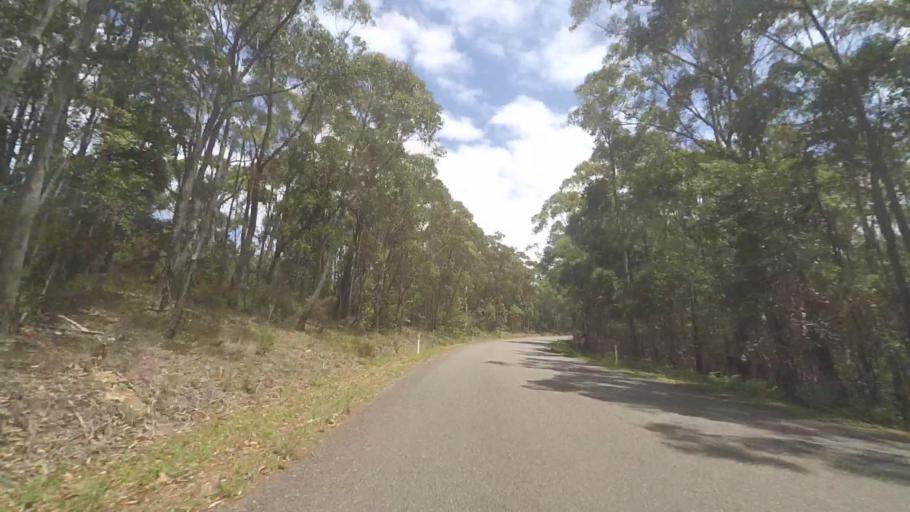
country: AU
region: New South Wales
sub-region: Shoalhaven Shire
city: Milton
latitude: -35.4013
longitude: 150.3651
